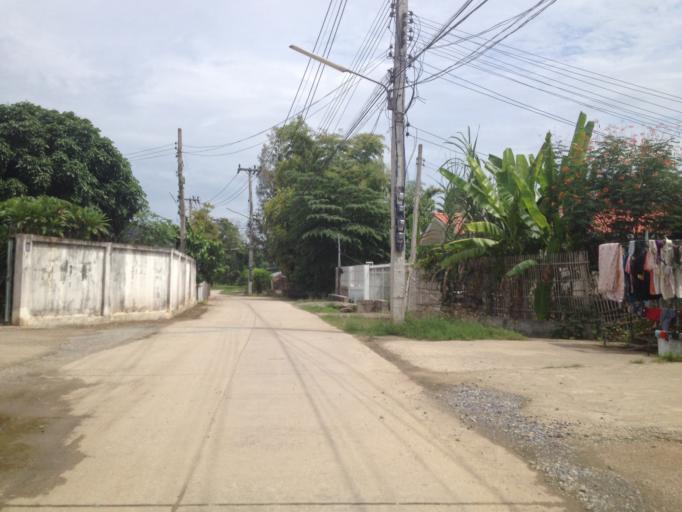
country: TH
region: Chiang Mai
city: Hang Dong
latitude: 18.7065
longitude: 98.9434
